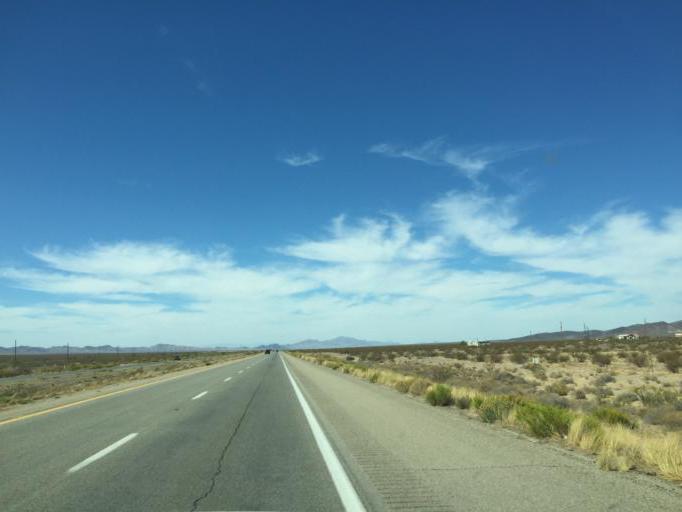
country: US
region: Arizona
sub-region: Mohave County
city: Dolan Springs
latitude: 35.5924
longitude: -114.3957
